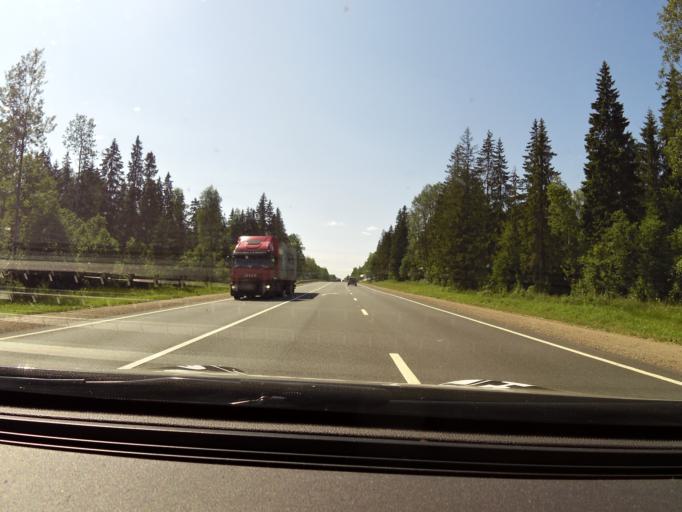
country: RU
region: Novgorod
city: Kresttsy
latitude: 58.3672
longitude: 32.1631
